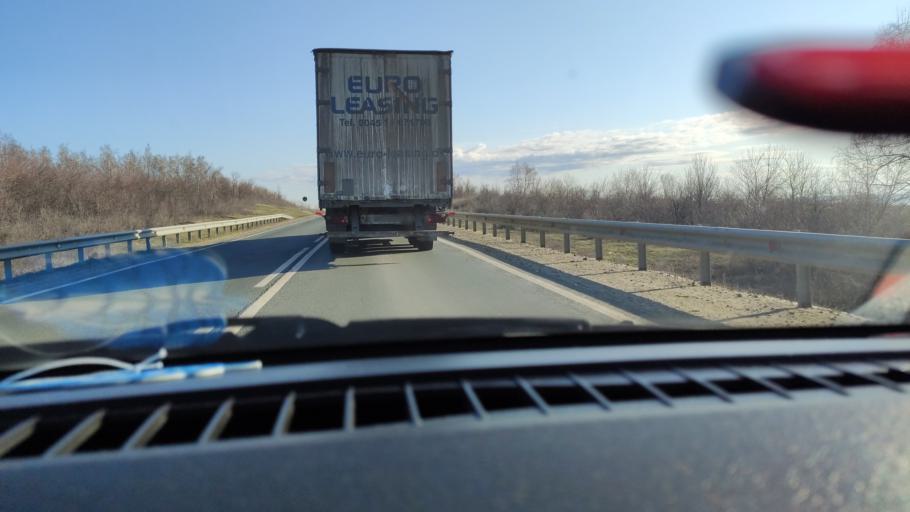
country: RU
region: Saratov
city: Dukhovnitskoye
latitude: 52.6784
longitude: 48.2300
